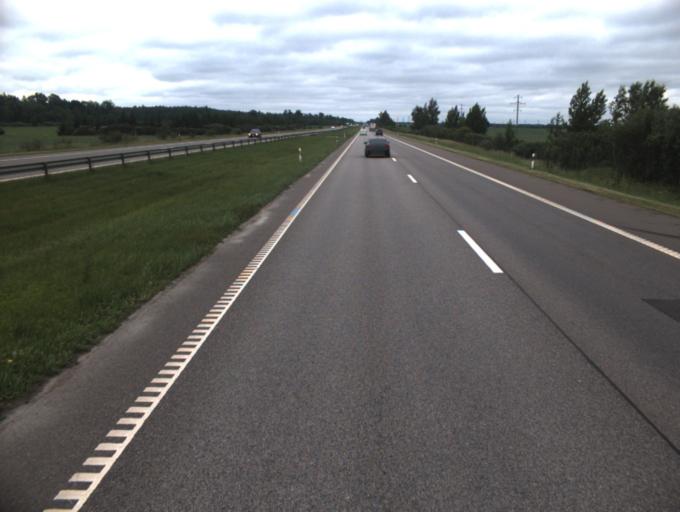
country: LT
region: Kauno apskritis
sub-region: Kaunas
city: Sargenai
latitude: 55.0314
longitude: 23.8272
